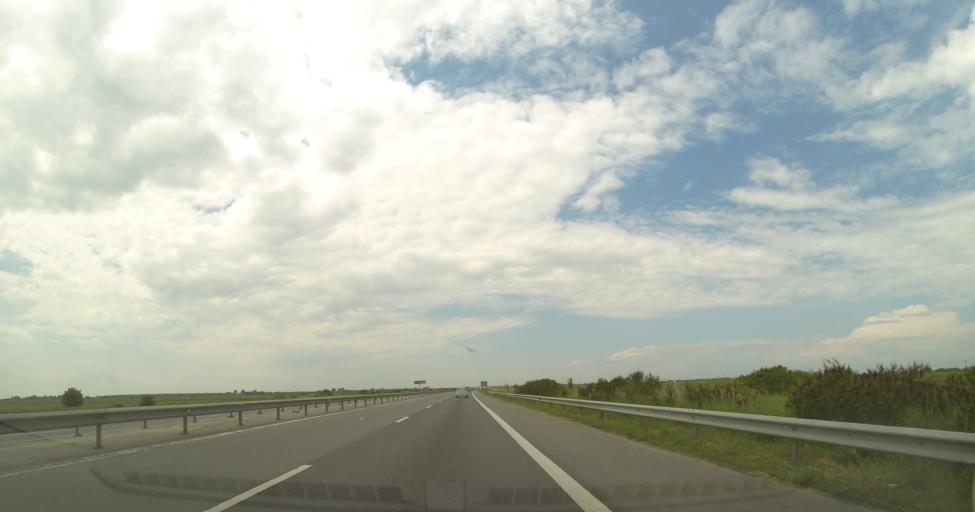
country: RO
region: Dambovita
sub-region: Comuna Mogosani
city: Zavoiu
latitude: 44.6263
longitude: 25.4249
